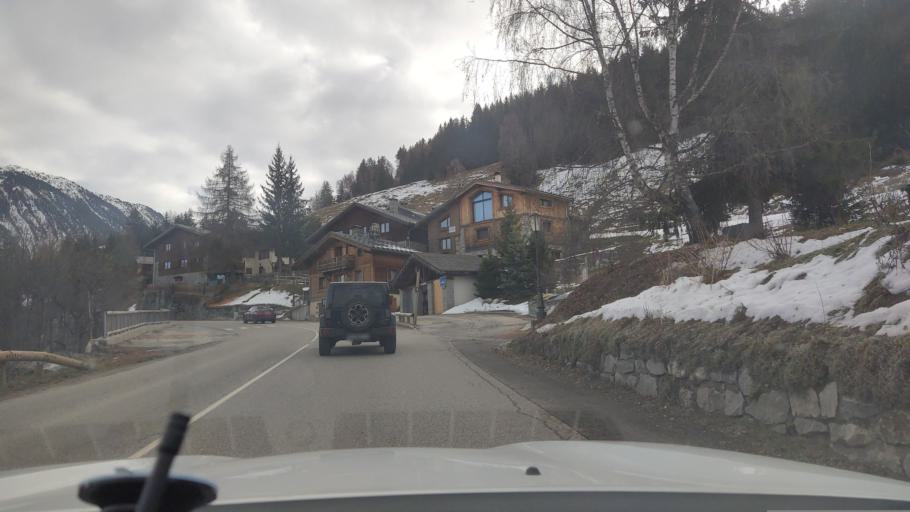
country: FR
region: Rhone-Alpes
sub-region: Departement de la Savoie
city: Saint-Bon-Tarentaise
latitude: 45.4282
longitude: 6.6341
